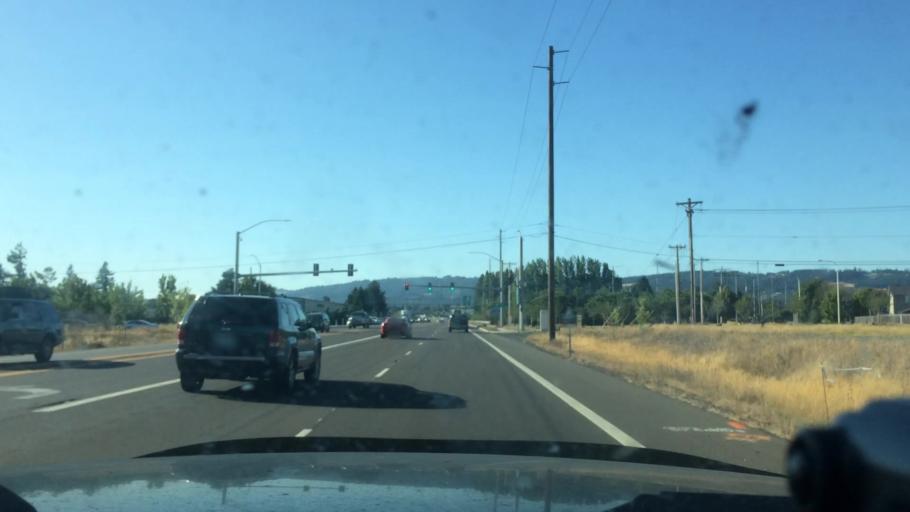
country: US
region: Oregon
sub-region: Yamhill County
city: Newberg
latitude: 45.2893
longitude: -122.9470
